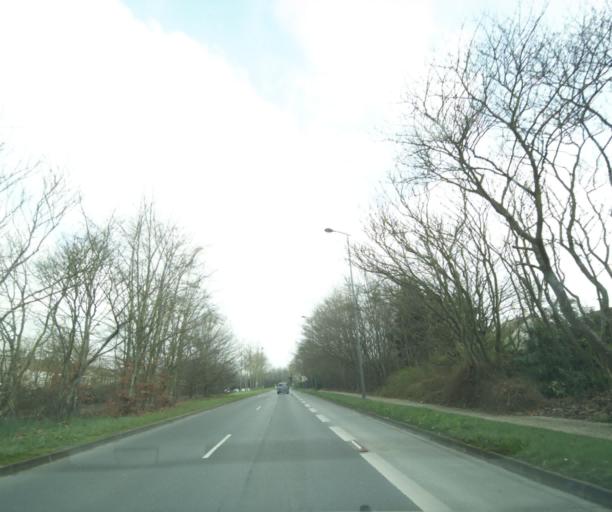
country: FR
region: Ile-de-France
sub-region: Departement du Val-d'Oise
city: Vaureal
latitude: 49.0453
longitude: 2.0206
